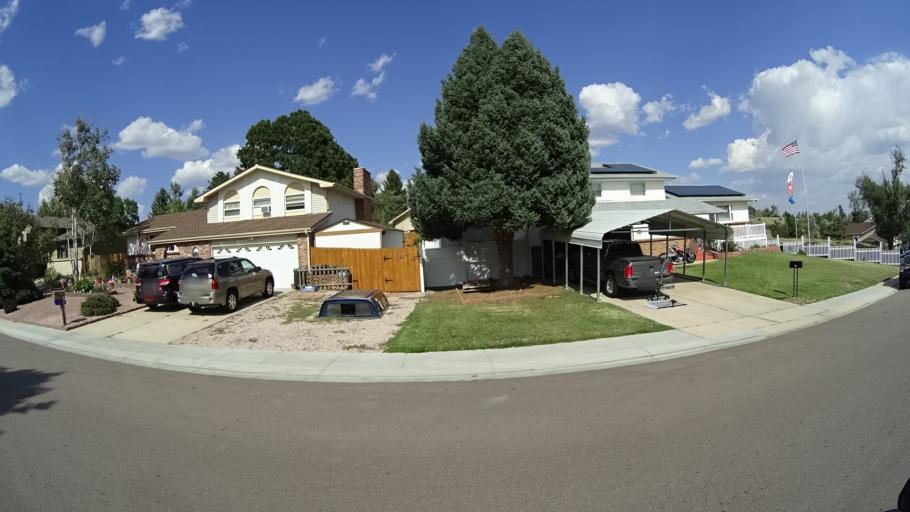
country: US
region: Colorado
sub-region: El Paso County
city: Cimarron Hills
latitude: 38.8730
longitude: -104.7316
